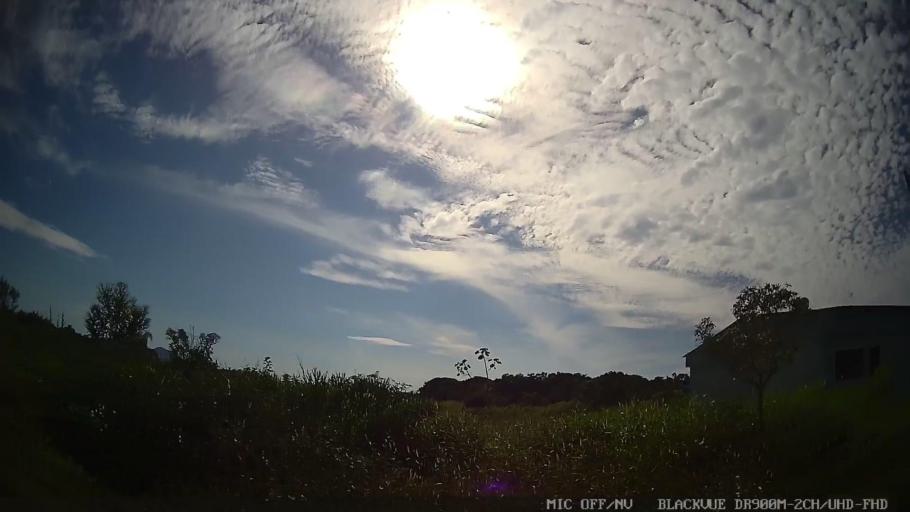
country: BR
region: Sao Paulo
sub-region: Iguape
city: Iguape
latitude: -24.7681
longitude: -47.5915
